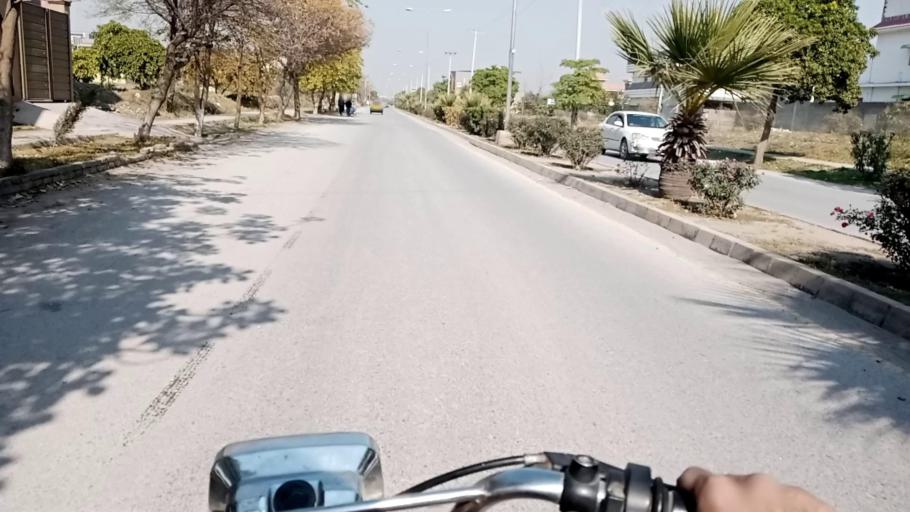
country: PK
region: Khyber Pakhtunkhwa
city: Peshawar
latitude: 33.9607
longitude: 71.4171
